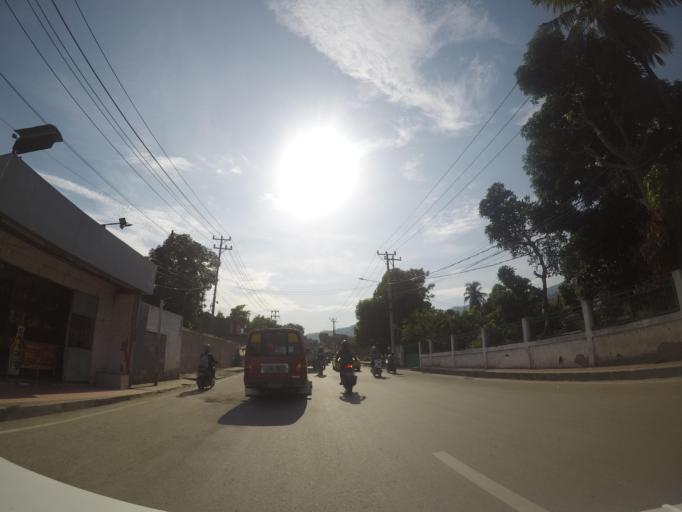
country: TL
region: Dili
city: Dili
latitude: -8.5608
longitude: 125.5994
